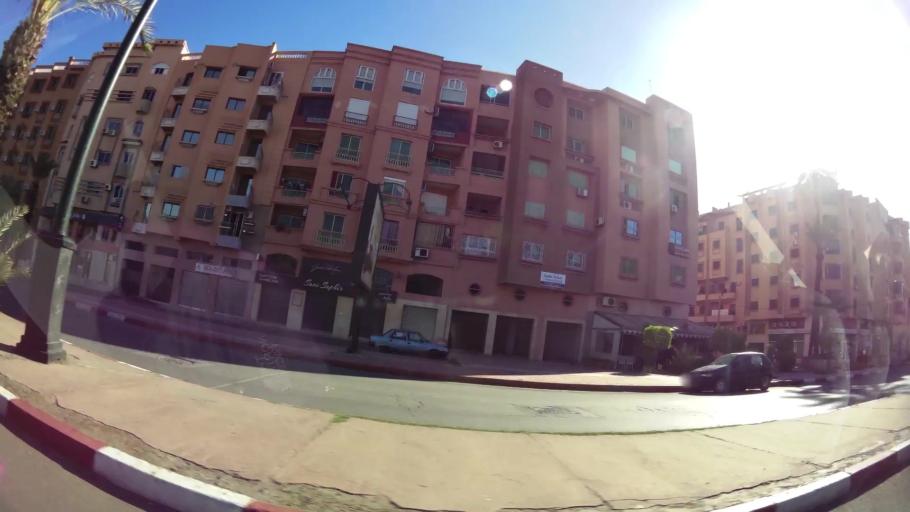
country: MA
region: Marrakech-Tensift-Al Haouz
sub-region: Marrakech
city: Marrakesh
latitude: 31.6529
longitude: -8.0177
